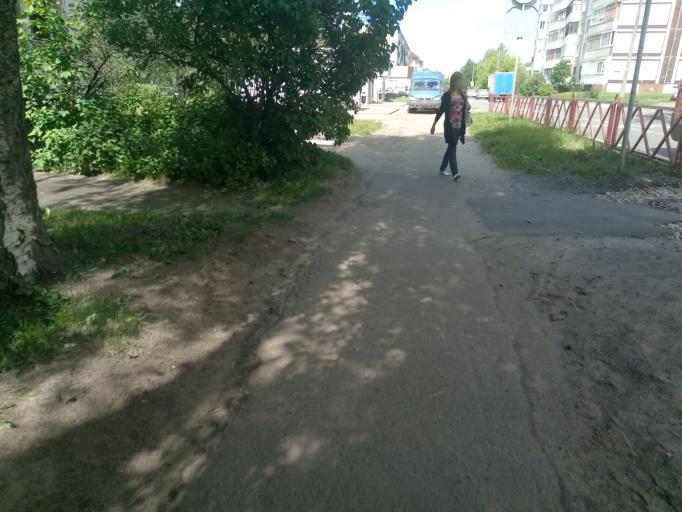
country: RU
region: Jaroslavl
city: Yaroslavl
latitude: 57.6555
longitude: 39.9590
